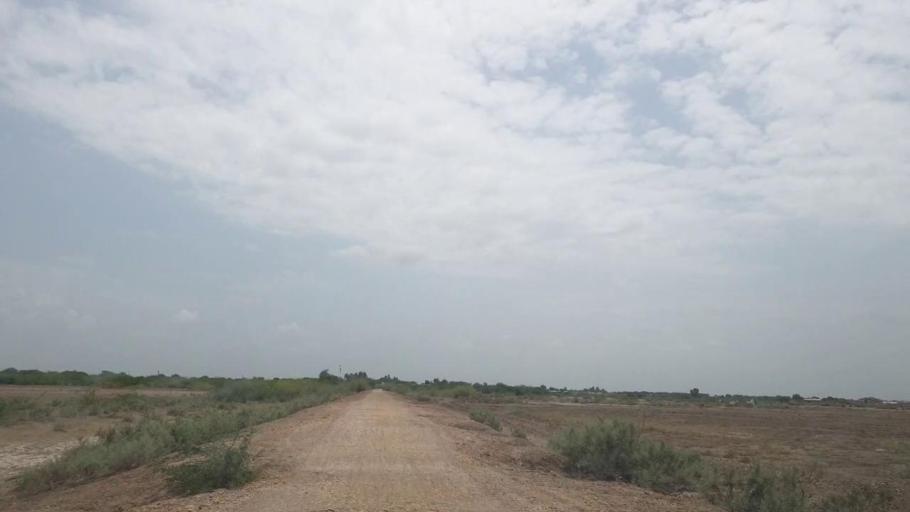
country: PK
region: Sindh
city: Naukot
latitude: 24.9107
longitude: 69.2030
